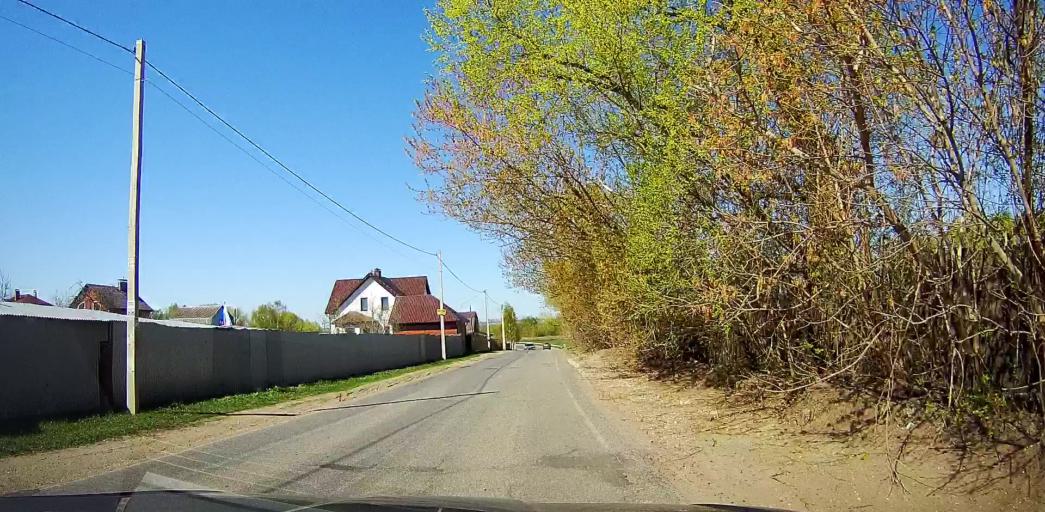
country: RU
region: Moskovskaya
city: Bronnitsy
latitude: 55.4900
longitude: 38.2382
